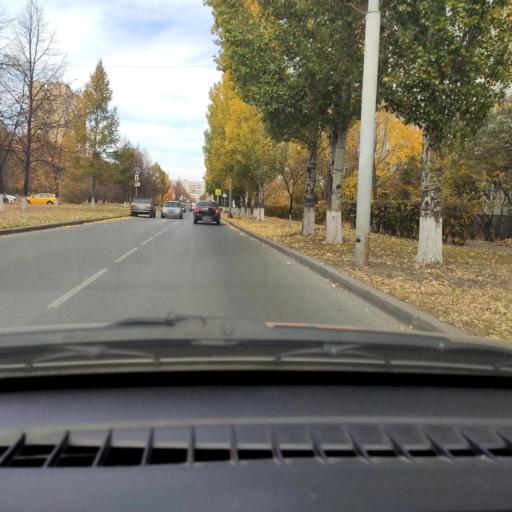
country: RU
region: Samara
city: Tol'yatti
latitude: 53.5347
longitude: 49.3208
